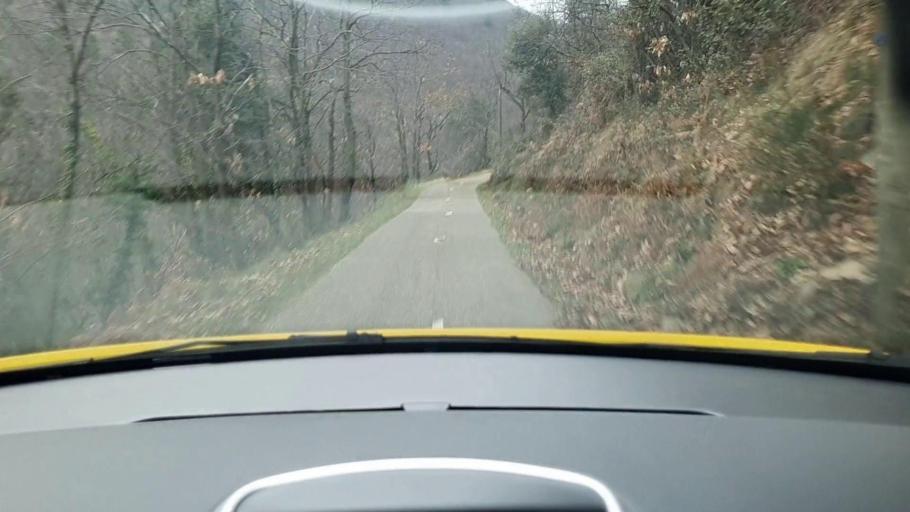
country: FR
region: Languedoc-Roussillon
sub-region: Departement du Gard
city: Besseges
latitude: 44.3714
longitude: 4.0407
